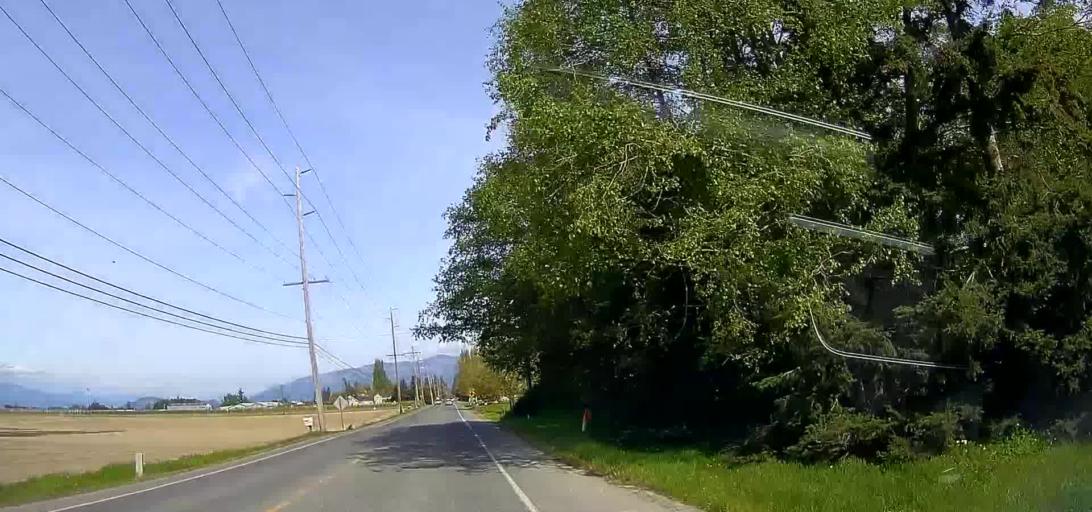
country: US
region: Washington
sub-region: Skagit County
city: Mount Vernon
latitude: 48.4208
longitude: -122.4259
